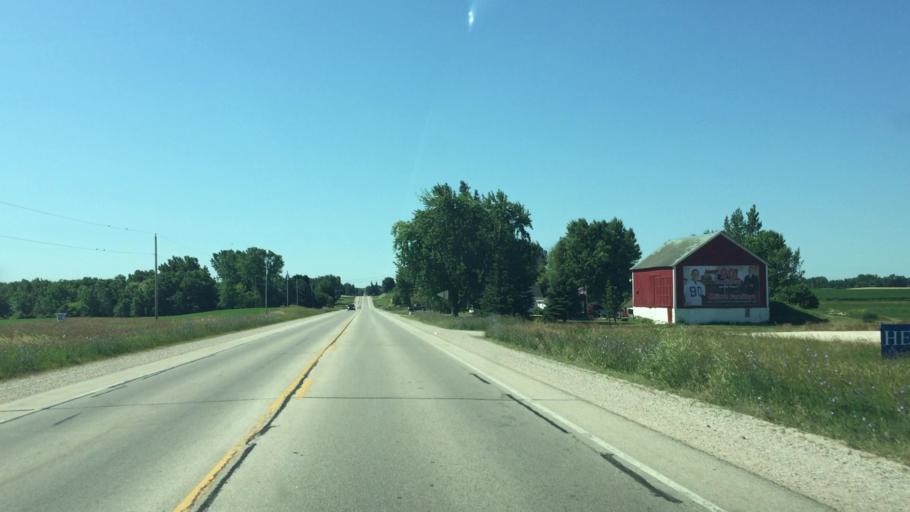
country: US
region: Wisconsin
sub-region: Calumet County
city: Chilton
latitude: 44.0541
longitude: -88.1630
